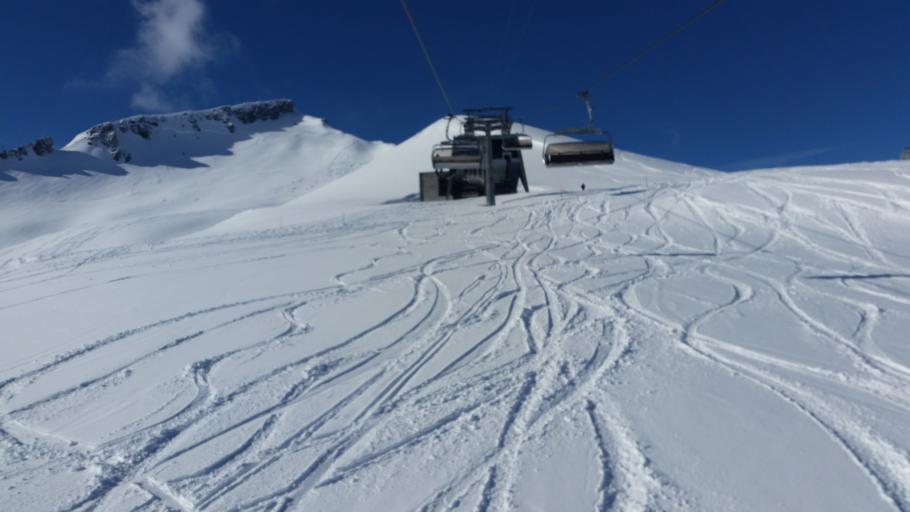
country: CH
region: Grisons
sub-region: Imboden District
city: Flims
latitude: 46.8682
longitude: 9.2212
